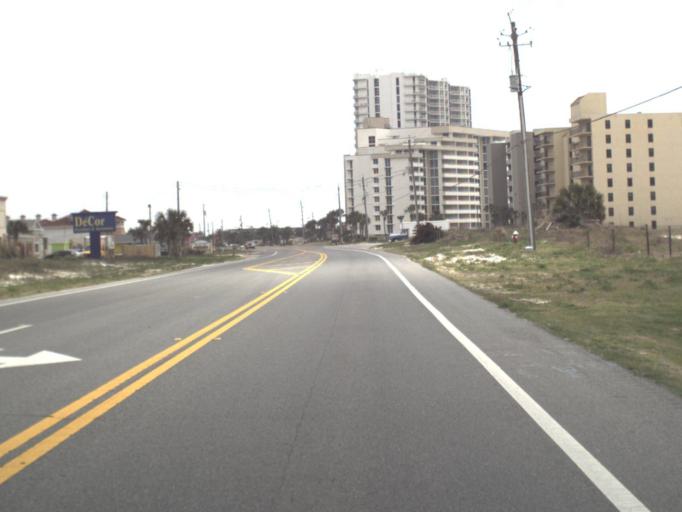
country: US
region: Alabama
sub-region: Baldwin County
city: Orange Beach
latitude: 30.2963
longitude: -87.4348
